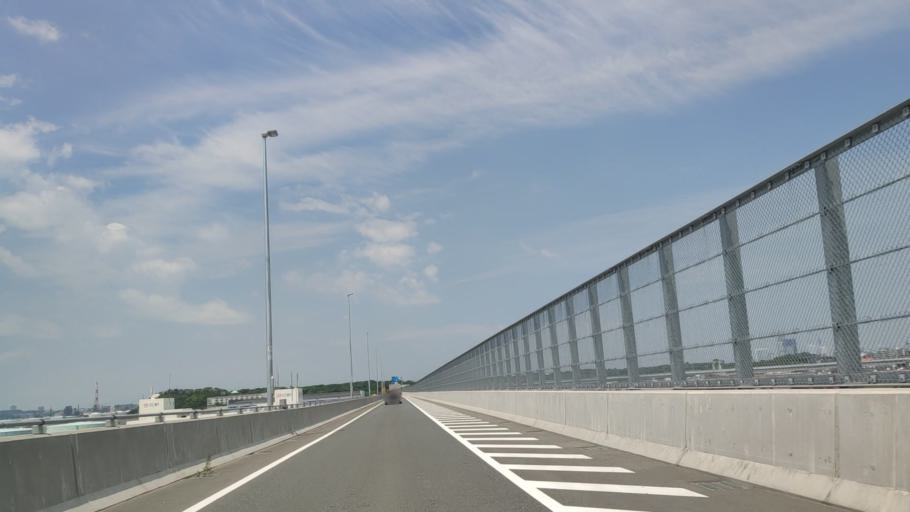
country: JP
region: Kanagawa
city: Yokohama
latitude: 35.4137
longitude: 139.6760
